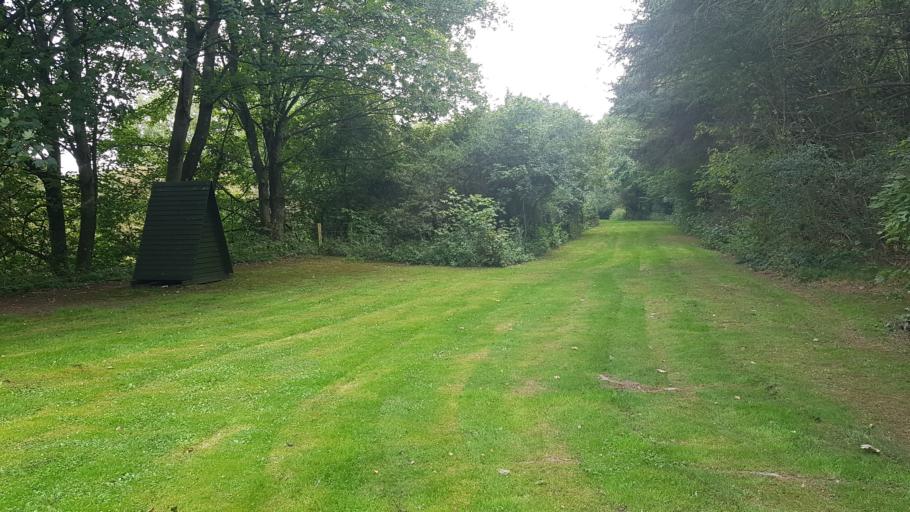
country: DK
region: South Denmark
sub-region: Aabenraa Kommune
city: Rodekro
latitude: 55.0585
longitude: 9.3415
